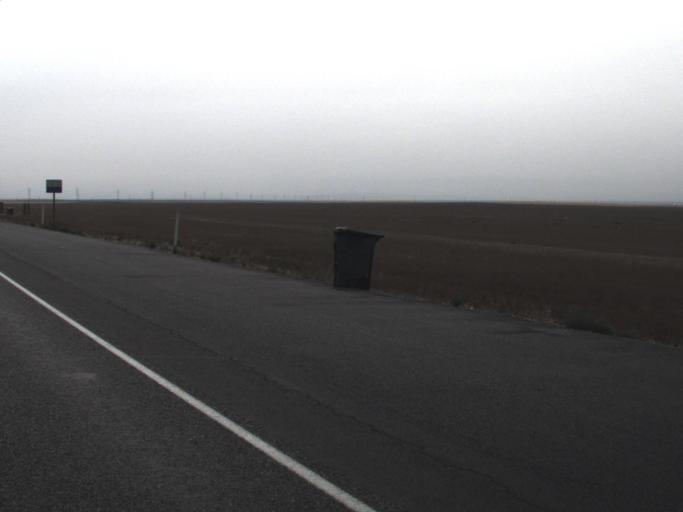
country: US
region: Washington
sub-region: Benton County
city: Benton City
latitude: 46.1150
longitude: -119.6018
